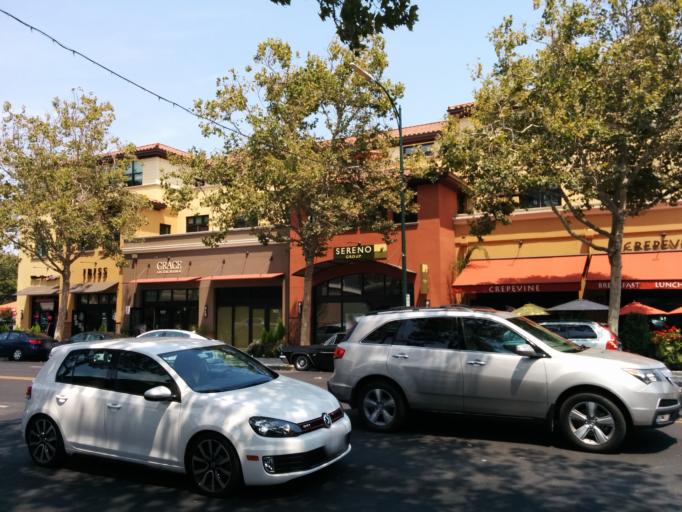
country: US
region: California
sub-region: Santa Clara County
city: Buena Vista
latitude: 37.3079
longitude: -121.9007
